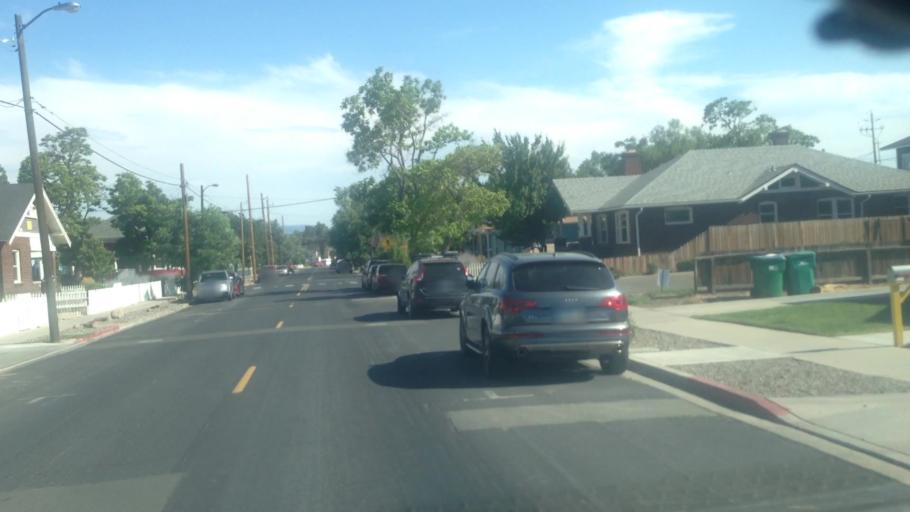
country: US
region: Nevada
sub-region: Washoe County
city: Reno
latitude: 39.5214
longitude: -119.8081
